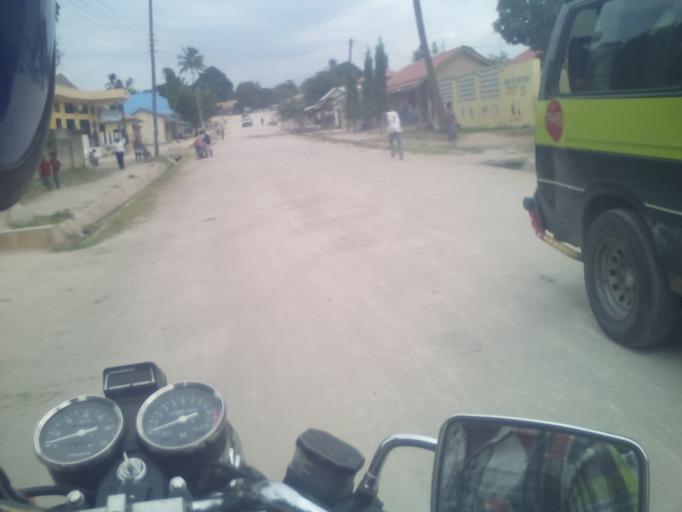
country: TZ
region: Dar es Salaam
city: Dar es Salaam
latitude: -6.8740
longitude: 39.2258
